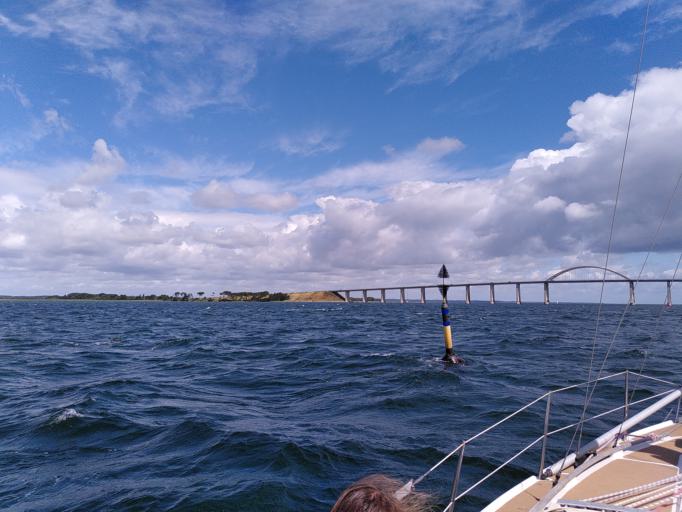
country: DK
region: South Denmark
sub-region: Langeland Kommune
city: Rudkobing
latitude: 54.9417
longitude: 10.7055
